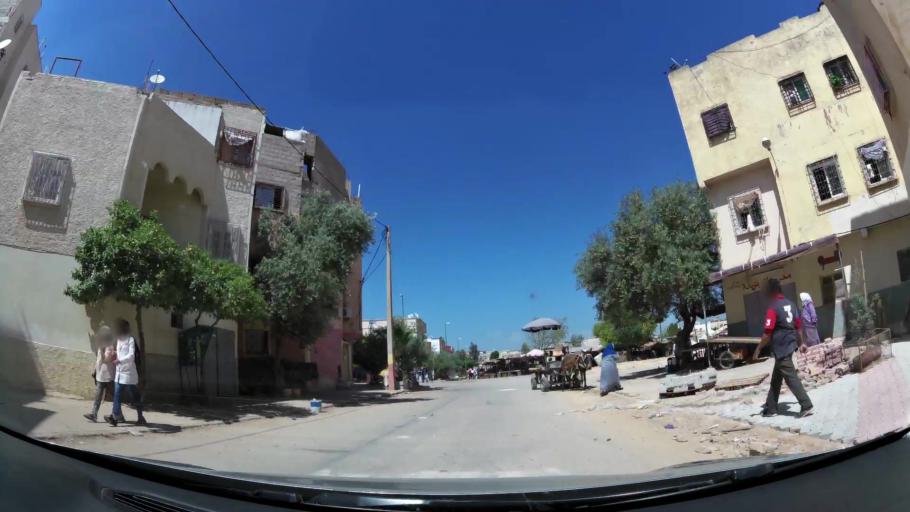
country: MA
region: Fes-Boulemane
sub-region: Fes
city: Fes
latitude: 34.0145
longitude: -5.0266
